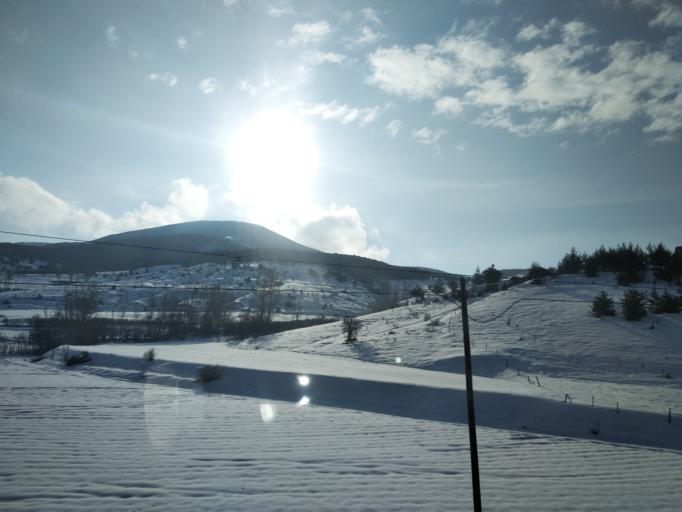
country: TR
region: Gumushane
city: Kelkit
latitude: 39.9838
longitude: 39.5393
